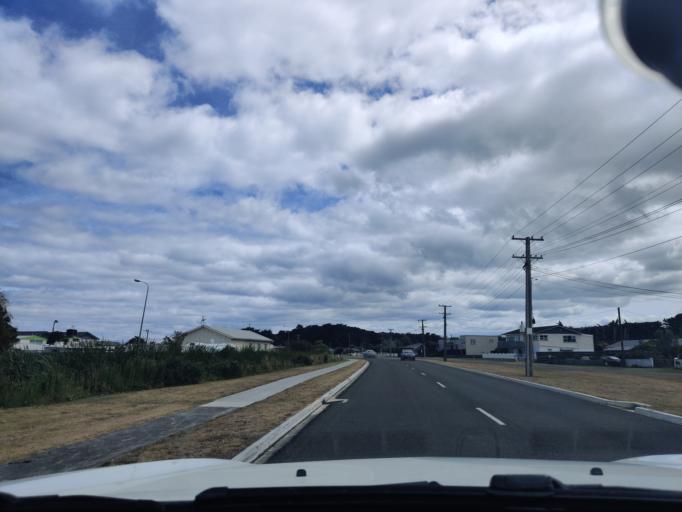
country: NZ
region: Manawatu-Wanganui
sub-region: Horowhenua District
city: Foxton
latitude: -40.4626
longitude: 175.2253
